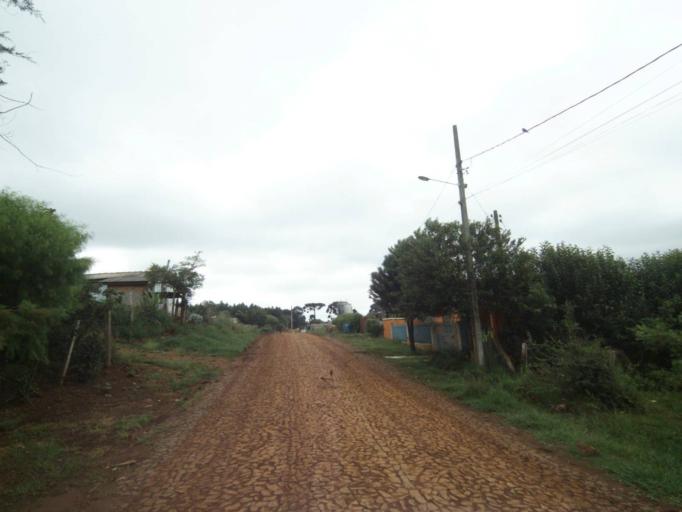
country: BR
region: Parana
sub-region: Pitanga
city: Pitanga
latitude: -24.9336
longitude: -51.8678
